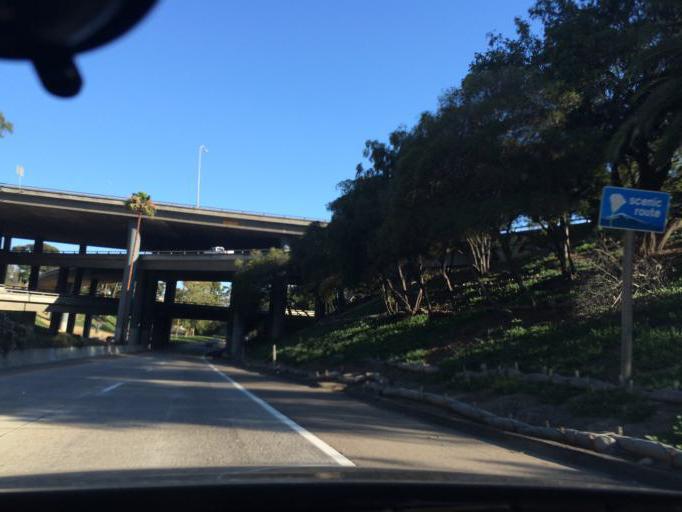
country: US
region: California
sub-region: San Diego County
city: San Diego
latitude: 32.7254
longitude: -117.1559
